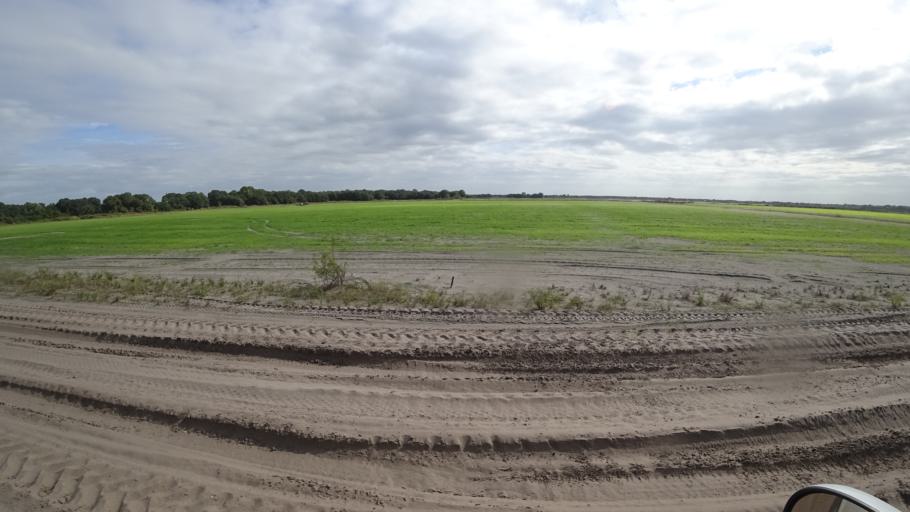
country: US
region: Florida
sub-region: Hillsborough County
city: Wimauma
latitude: 27.5687
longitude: -82.3121
